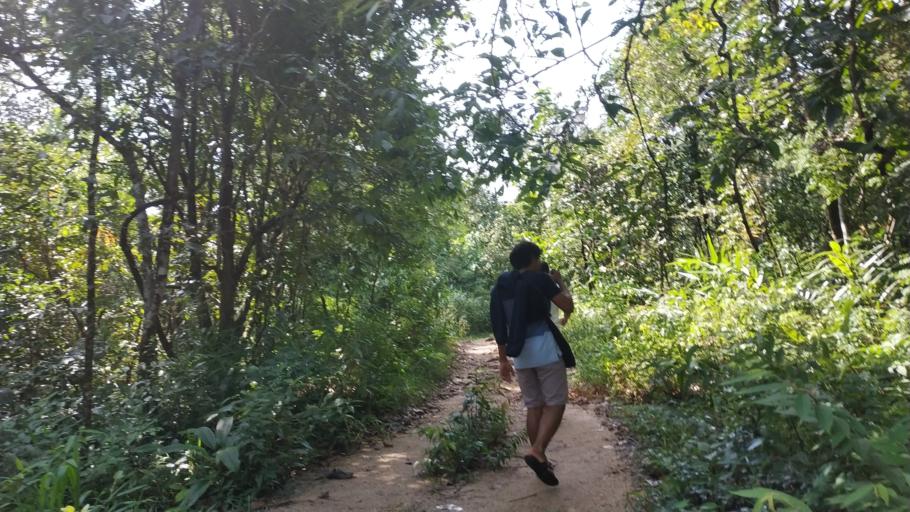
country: MM
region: Tanintharyi
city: Dawei
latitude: 14.5848
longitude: 98.0495
